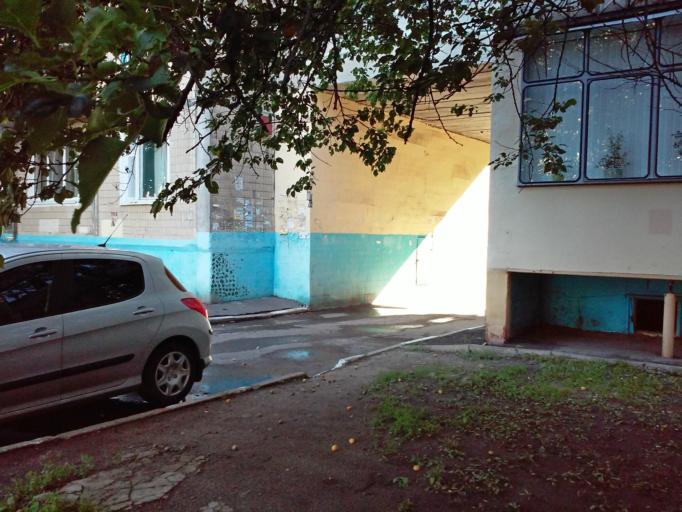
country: RU
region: Belgorod
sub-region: Belgorodskiy Rayon
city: Belgorod
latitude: 50.5625
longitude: 36.5672
